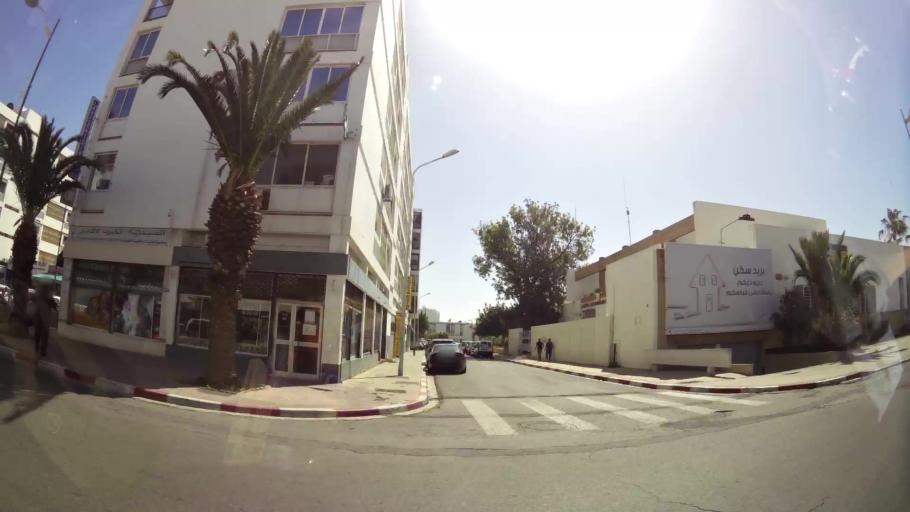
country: MA
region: Souss-Massa-Draa
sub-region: Agadir-Ida-ou-Tnan
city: Agadir
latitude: 30.4208
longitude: -9.5972
